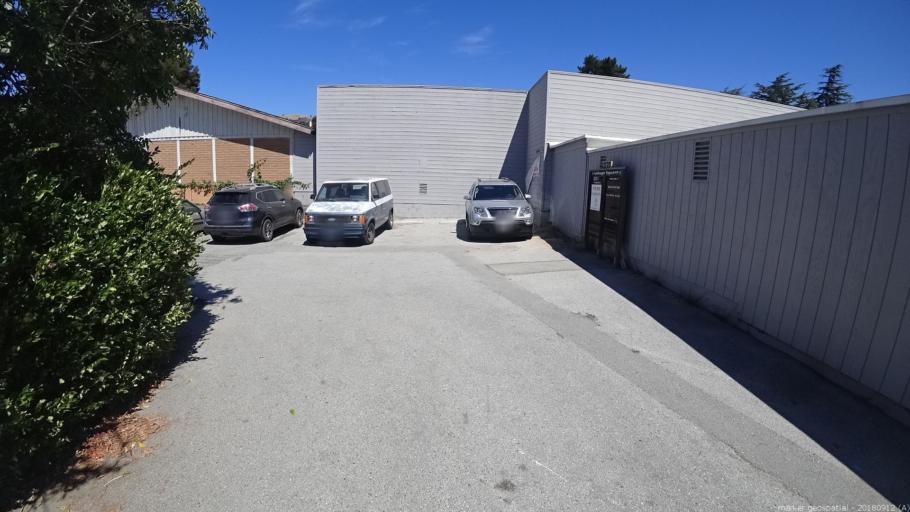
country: US
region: California
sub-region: Monterey County
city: Carmel Valley Village
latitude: 36.4787
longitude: -121.7314
